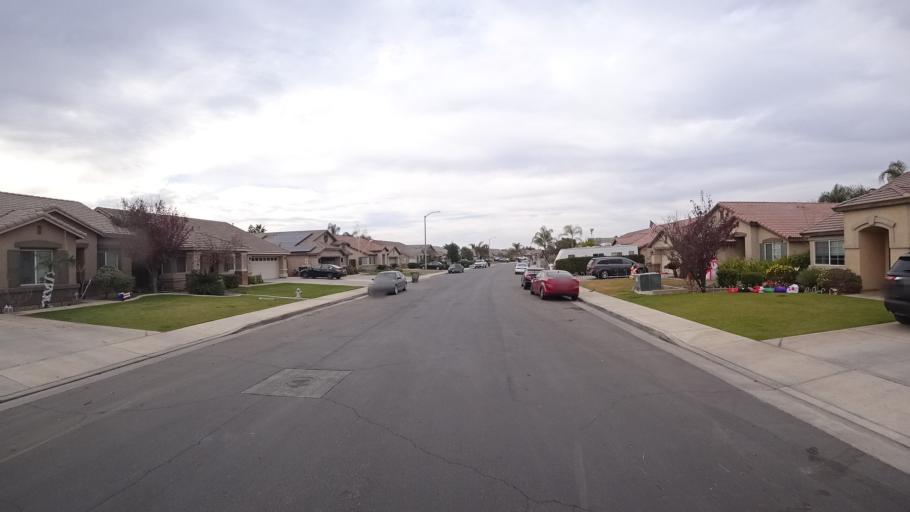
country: US
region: California
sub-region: Kern County
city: Rosedale
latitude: 35.4067
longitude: -119.1482
